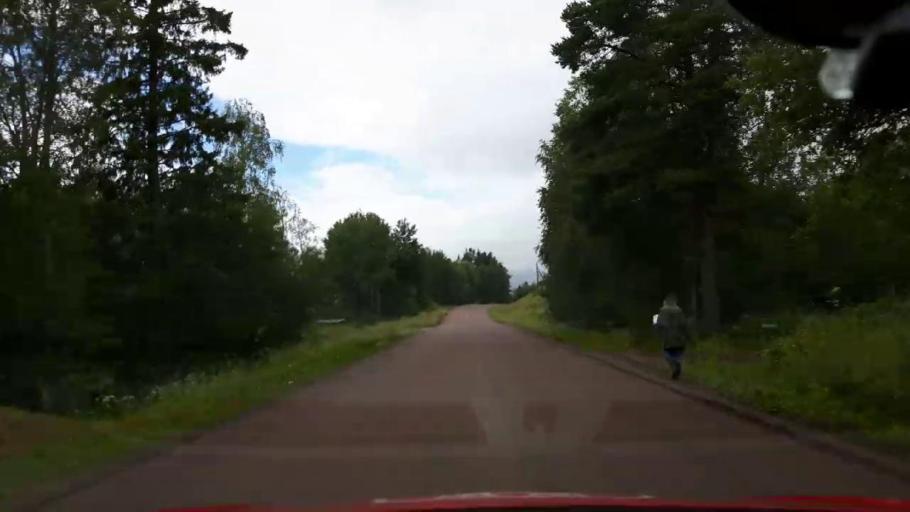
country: SE
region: Jaemtland
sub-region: Krokoms Kommun
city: Valla
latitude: 63.3753
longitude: 14.0211
